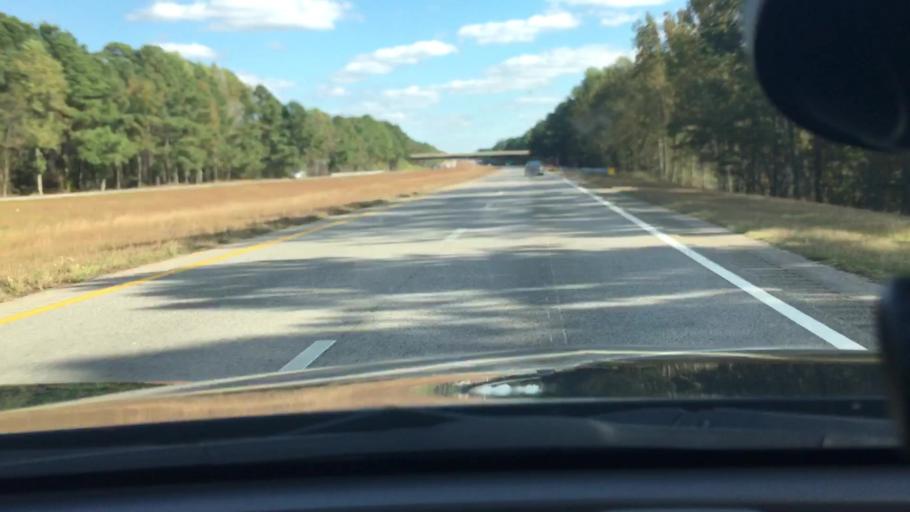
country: US
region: North Carolina
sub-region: Wilson County
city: Lucama
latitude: 35.7790
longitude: -78.0782
